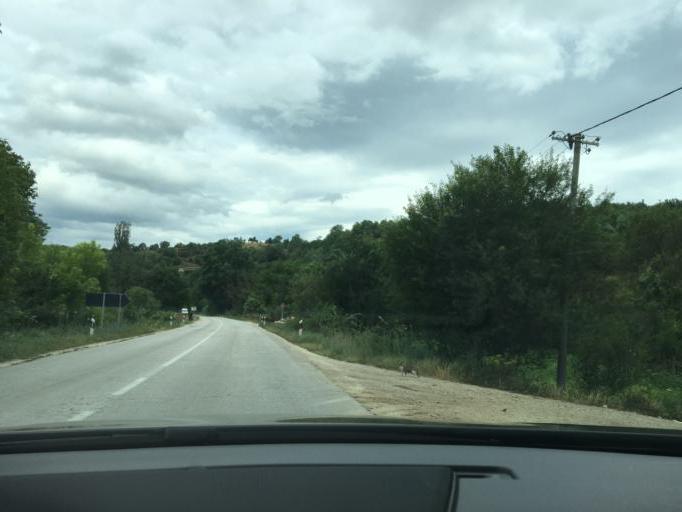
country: MK
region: Kriva Palanka
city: Kriva Palanka
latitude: 42.1766
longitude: 22.2439
